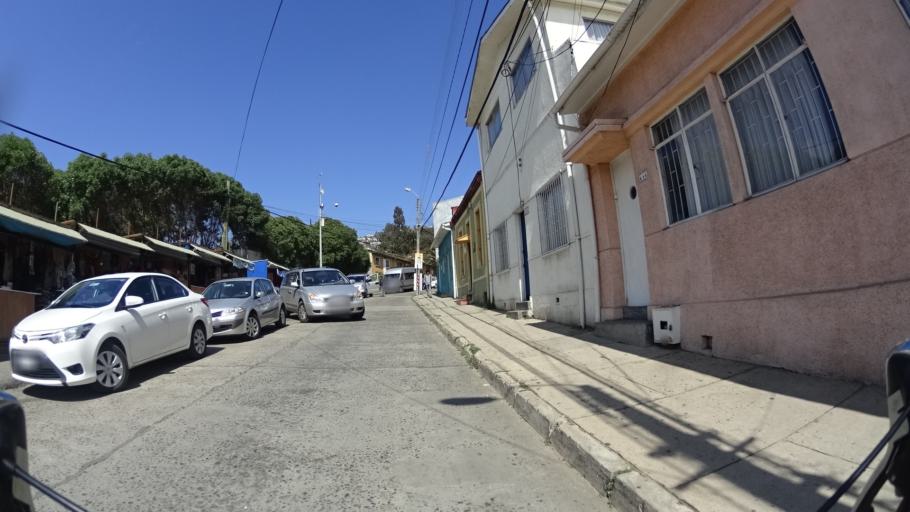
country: CL
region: Valparaiso
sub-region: Provincia de Valparaiso
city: Valparaiso
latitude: -33.0534
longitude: -71.6223
